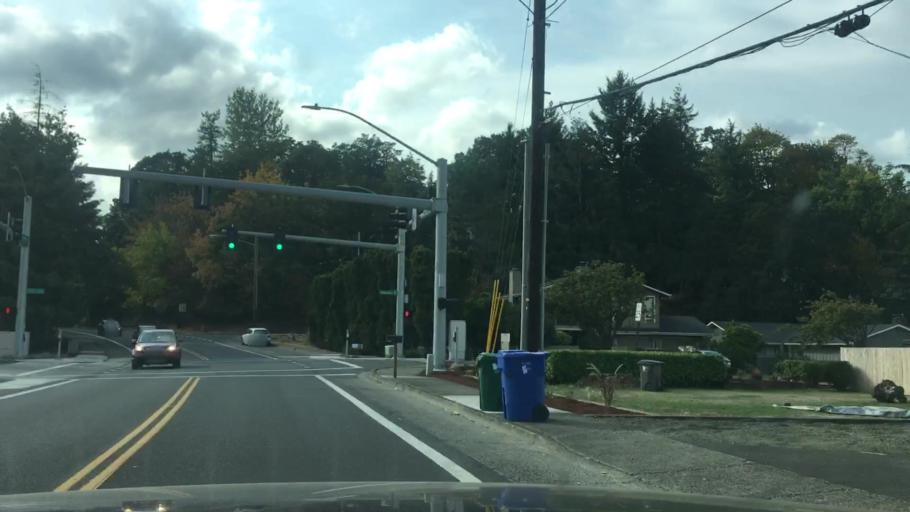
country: US
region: Oregon
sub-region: Lane County
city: Eugene
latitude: 44.0841
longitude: -123.0940
